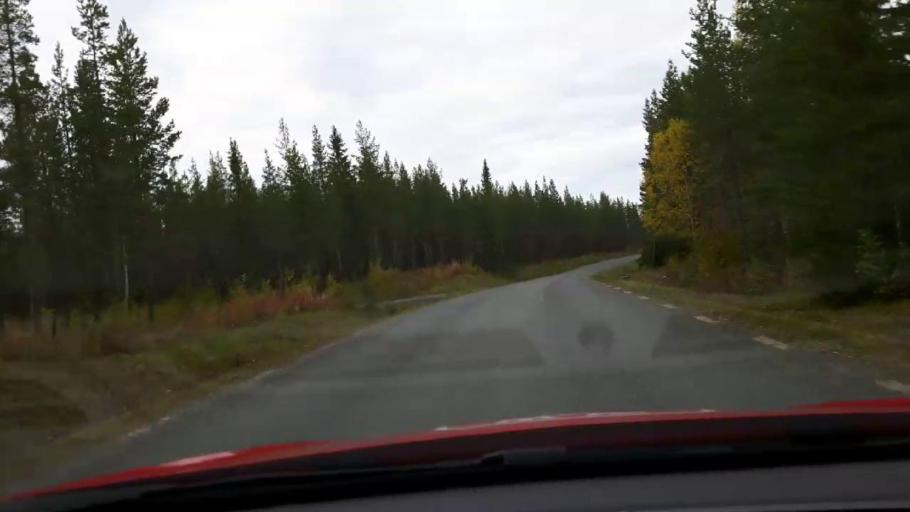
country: SE
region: Jaemtland
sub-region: Krokoms Kommun
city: Krokom
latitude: 63.2124
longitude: 14.1171
